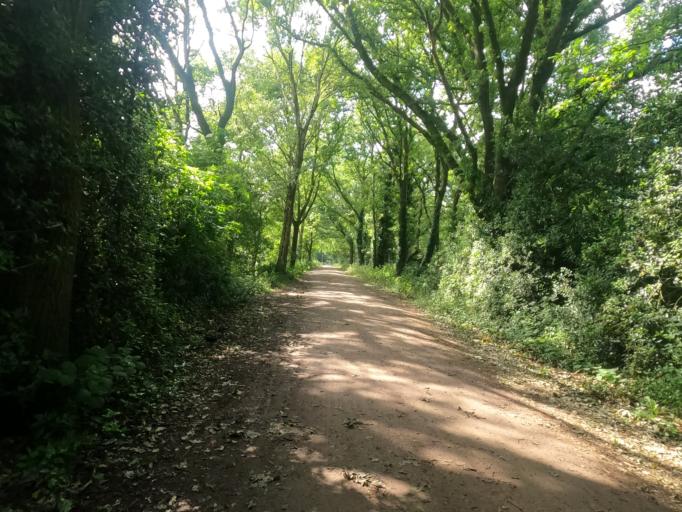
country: GB
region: England
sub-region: Cheshire West and Chester
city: Cuddington
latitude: 53.2111
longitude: -2.5887
